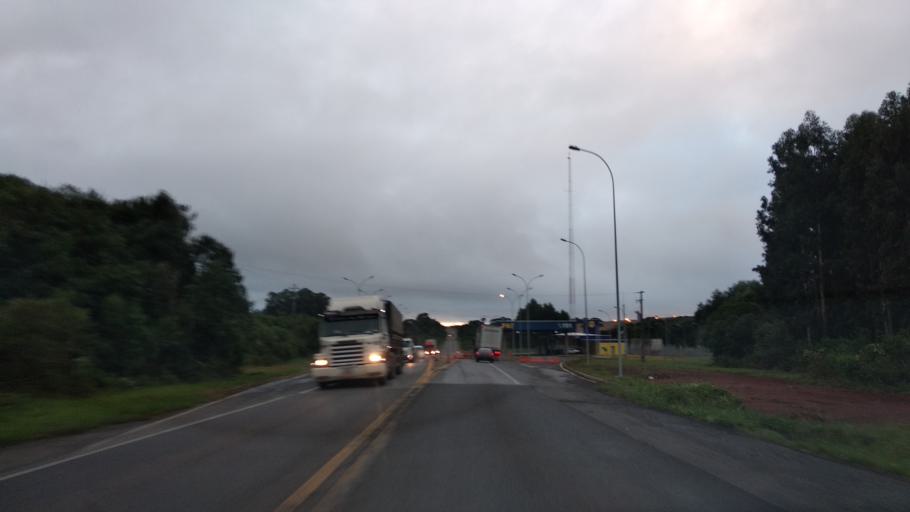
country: BR
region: Santa Catarina
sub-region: Campos Novos
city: Campos Novos
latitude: -27.3878
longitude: -51.1155
